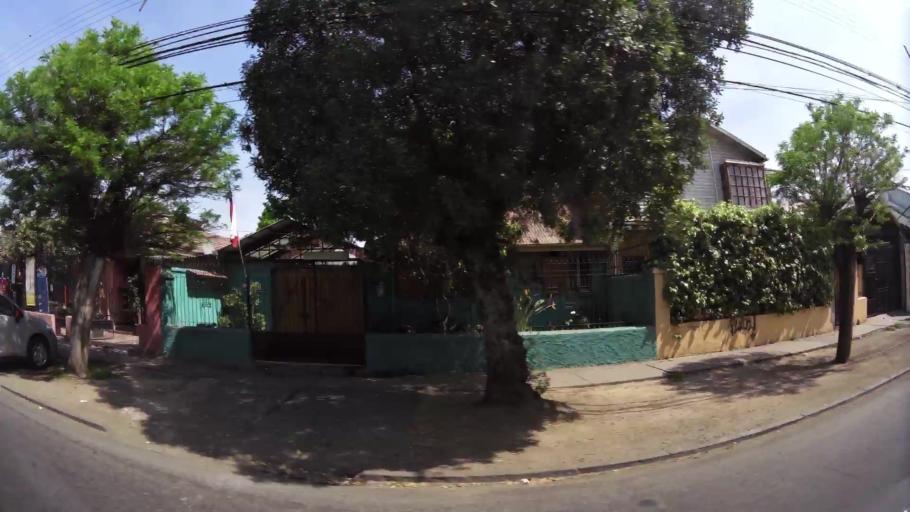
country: CL
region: Santiago Metropolitan
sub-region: Provincia de Santiago
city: Lo Prado
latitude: -33.4207
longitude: -70.6978
